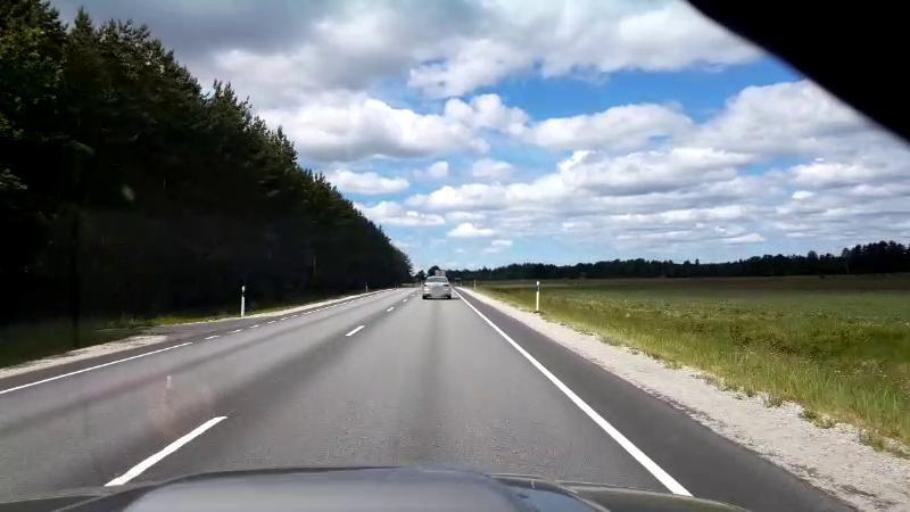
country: EE
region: Paernumaa
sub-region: Halinga vald
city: Parnu-Jaagupi
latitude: 58.6650
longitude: 24.4603
